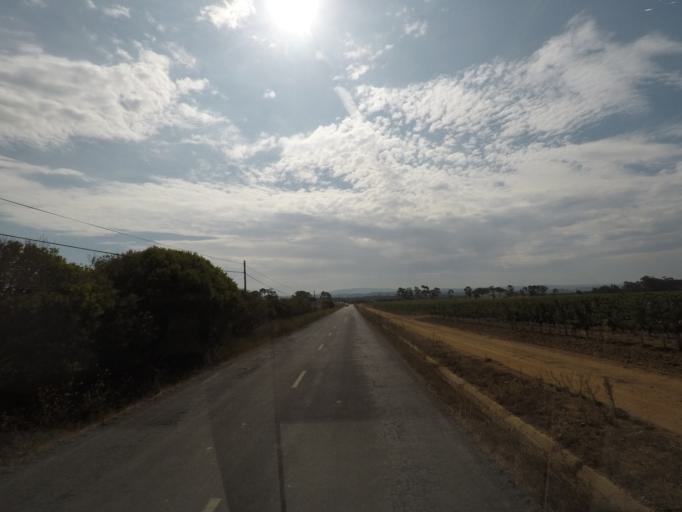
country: PT
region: Beja
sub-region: Odemira
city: Sao Teotonio
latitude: 37.4695
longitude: -8.7534
